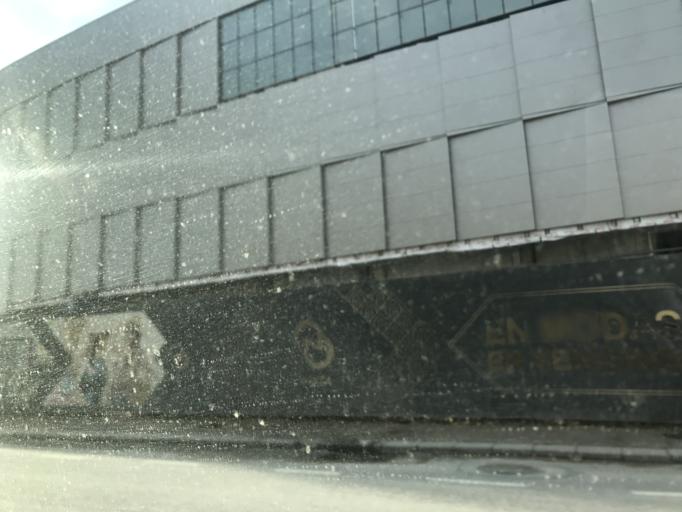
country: TR
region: Ankara
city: Mamak
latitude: 39.9754
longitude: 32.8848
